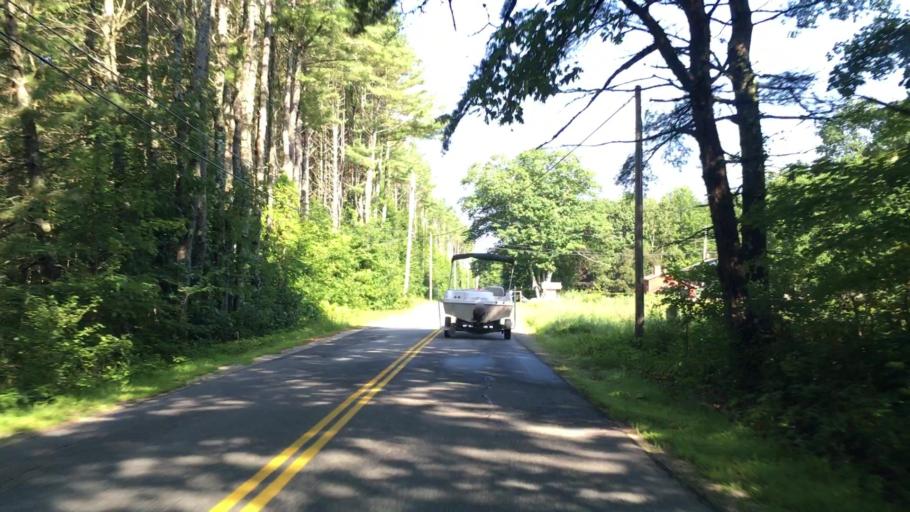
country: US
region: Maine
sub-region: Androscoggin County
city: Poland
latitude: 44.0583
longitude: -70.3824
